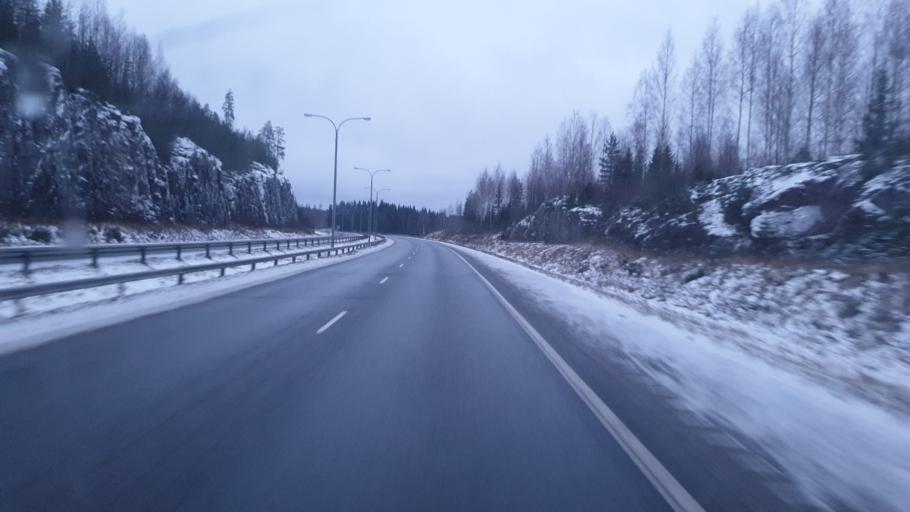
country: FI
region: Northern Savo
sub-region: Kuopio
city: Siilinjaervi
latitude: 63.0374
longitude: 27.6586
